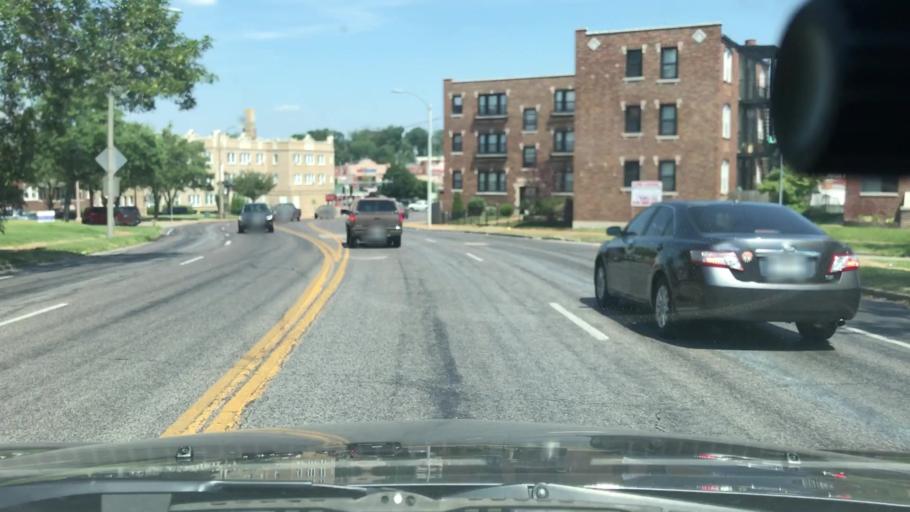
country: US
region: Missouri
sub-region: Saint Louis County
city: Maplewood
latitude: 38.5914
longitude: -90.2751
